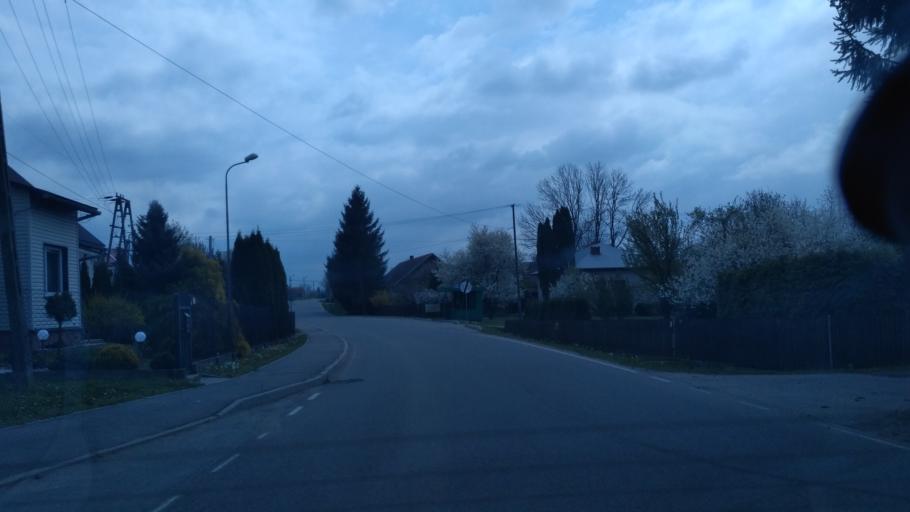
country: PL
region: Subcarpathian Voivodeship
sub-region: Powiat brzozowski
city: Haczow
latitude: 49.6622
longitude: 21.9046
